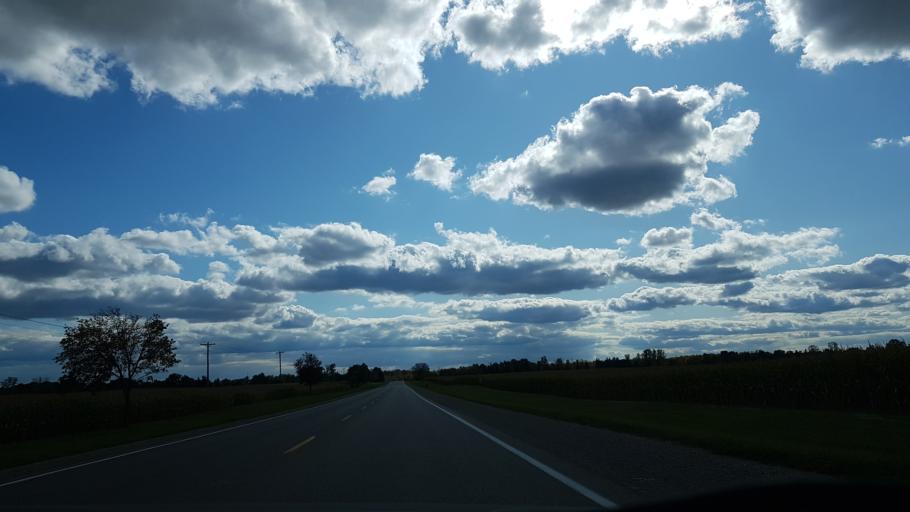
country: CA
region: Ontario
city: South Huron
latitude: 43.1853
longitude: -81.6773
